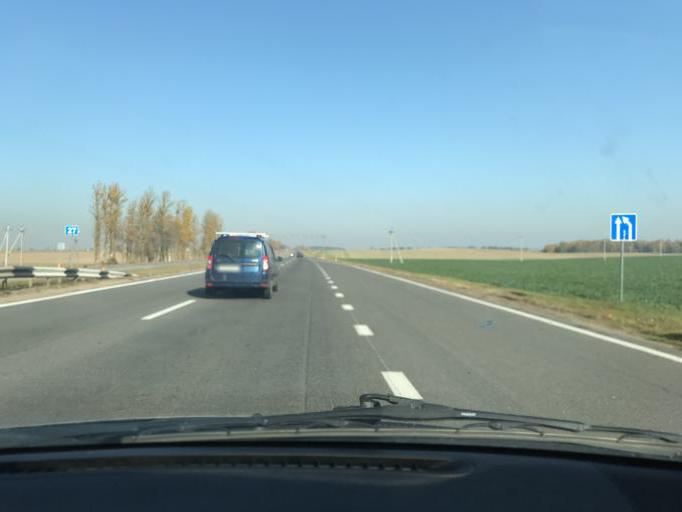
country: BY
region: Minsk
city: Samakhvalavichy
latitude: 53.6787
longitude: 27.5030
